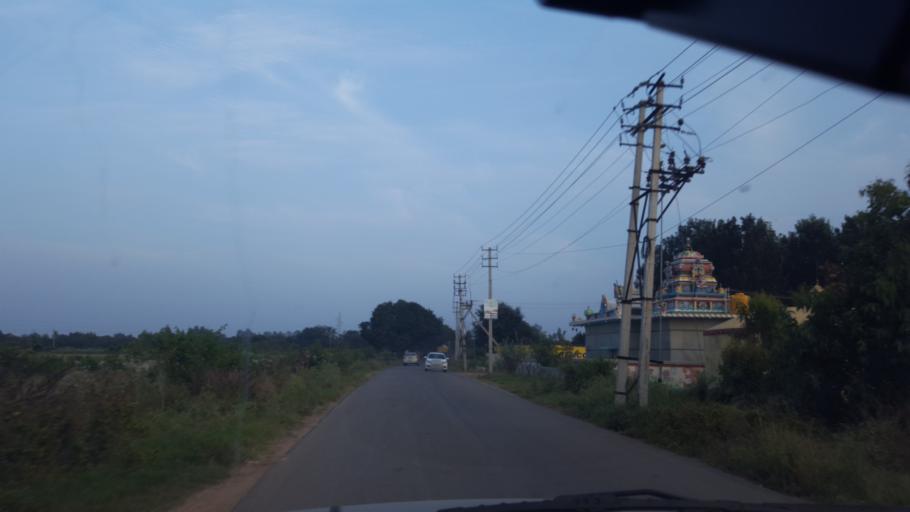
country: IN
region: Karnataka
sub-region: Bangalore Urban
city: Yelahanka
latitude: 13.0782
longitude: 77.6943
